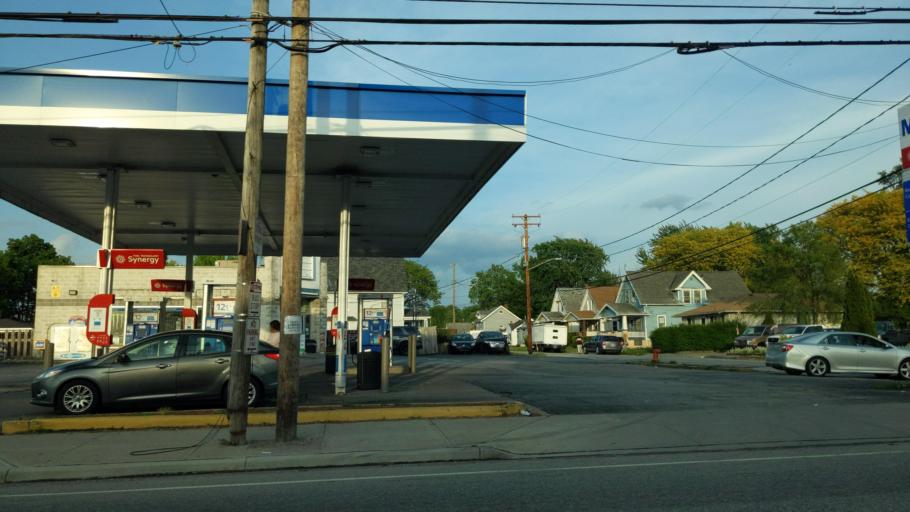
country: US
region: Ohio
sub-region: Cuyahoga County
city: Brook Park
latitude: 41.4288
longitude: -81.7801
